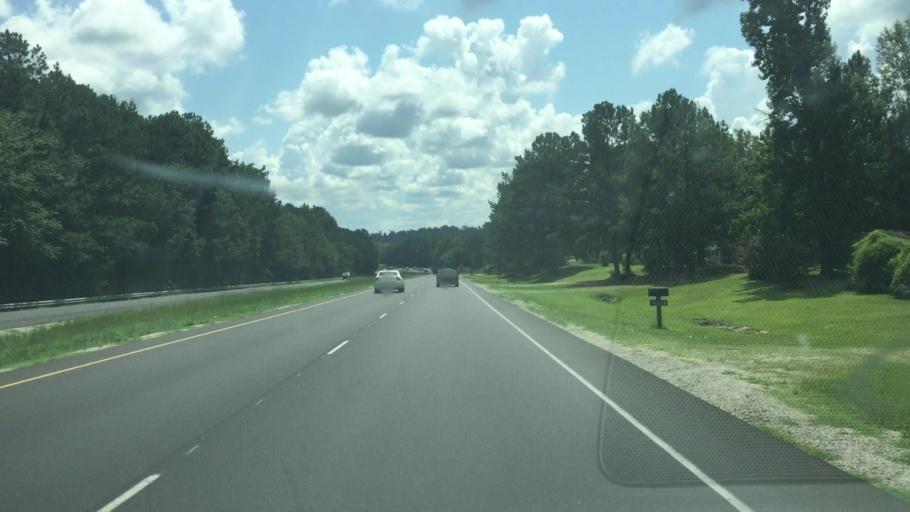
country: US
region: North Carolina
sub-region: Richmond County
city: Cordova
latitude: 34.9458
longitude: -79.8936
